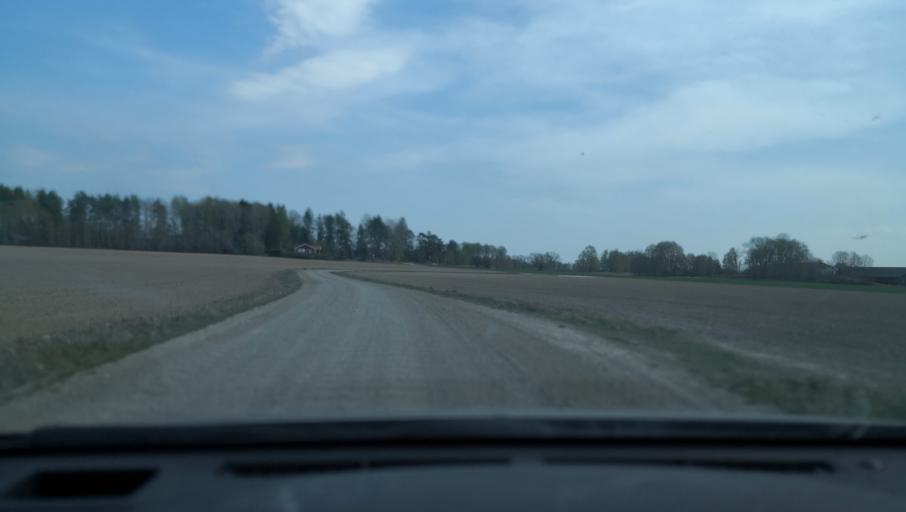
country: SE
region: Vaestmanland
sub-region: Vasteras
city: Skultuna
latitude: 59.7816
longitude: 16.4535
